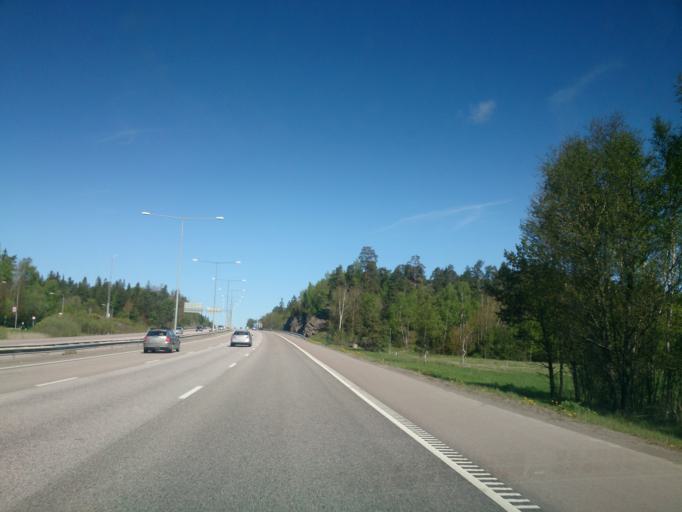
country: SE
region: Stockholm
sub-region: Haninge Kommun
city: Haninge
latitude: 59.1880
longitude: 18.1475
